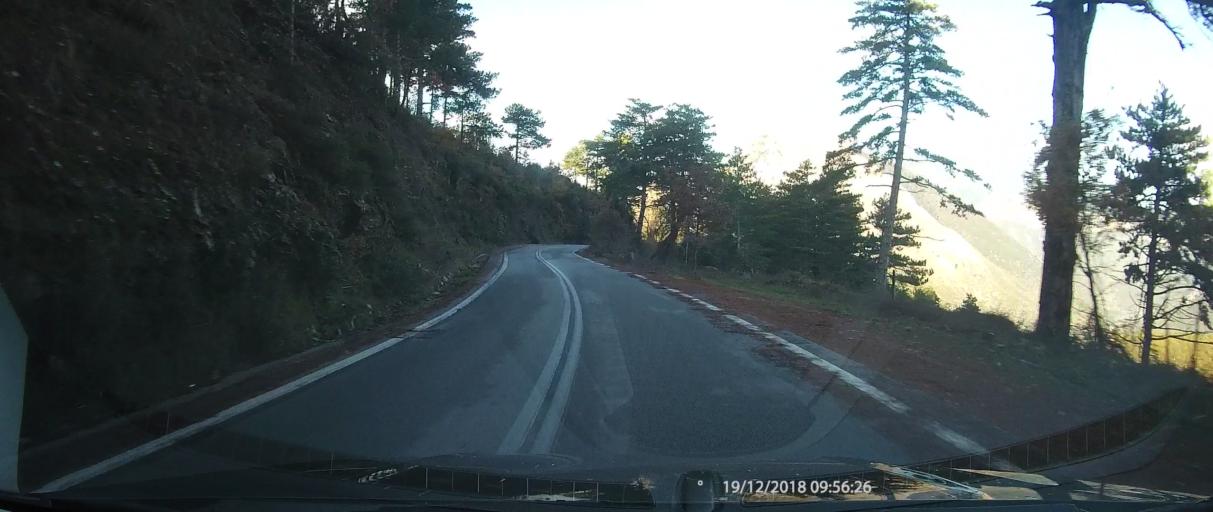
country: GR
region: Peloponnese
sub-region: Nomos Messinias
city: Paralia Vergas
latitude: 37.0858
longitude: 22.2393
